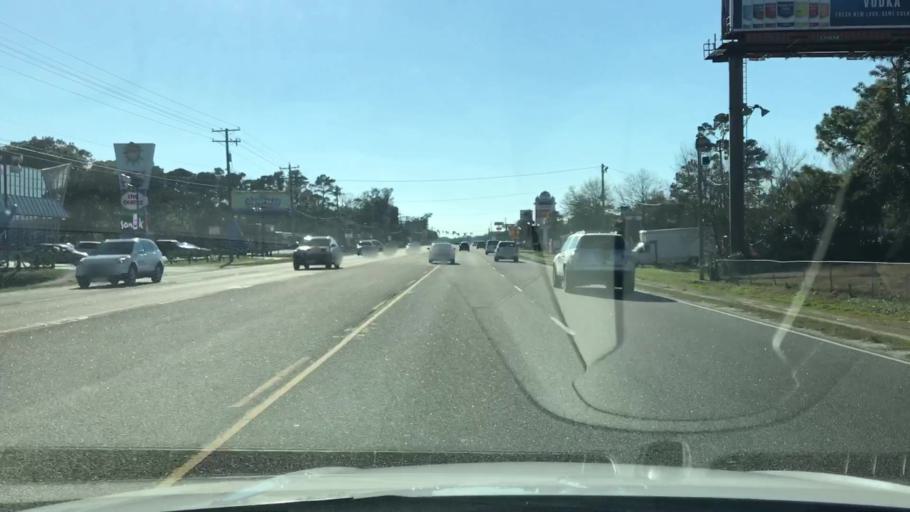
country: US
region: South Carolina
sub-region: Horry County
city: Garden City
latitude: 33.5819
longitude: -79.0181
